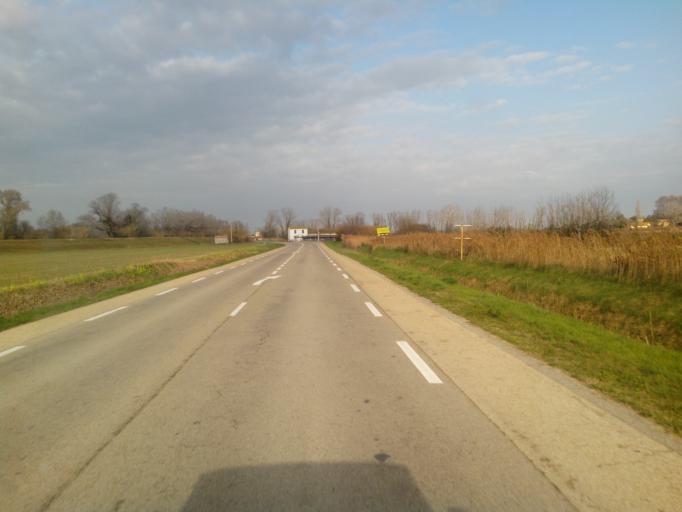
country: FR
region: Languedoc-Roussillon
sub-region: Departement du Gard
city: Saint-Gilles
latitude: 43.6012
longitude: 4.4740
